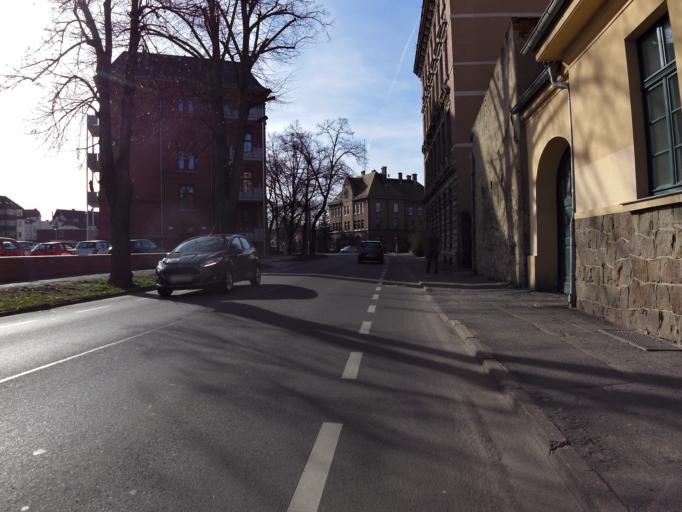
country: DE
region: Saxony
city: Torgau
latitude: 51.5612
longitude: 13.0025
